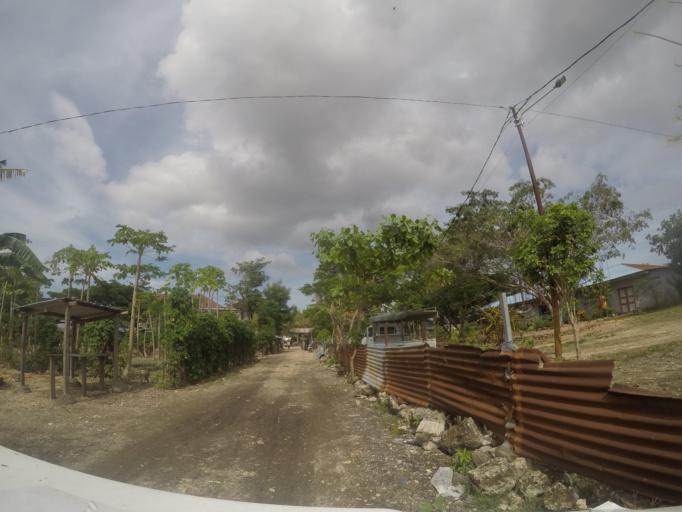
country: TL
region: Baucau
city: Baucau
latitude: -8.4805
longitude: 126.4531
